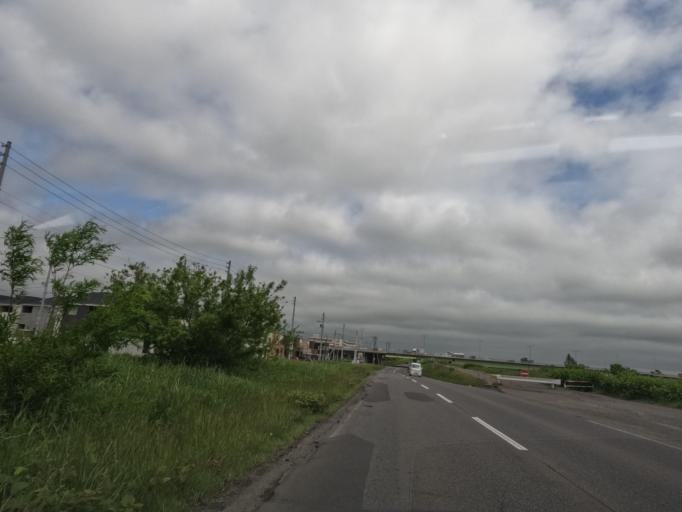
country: JP
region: Hokkaido
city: Sapporo
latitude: 43.0926
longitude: 141.4341
